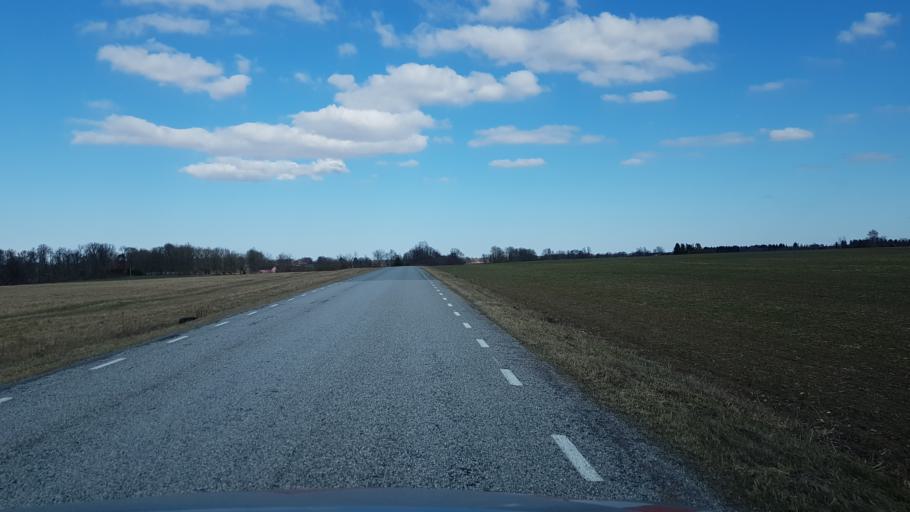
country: EE
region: Laeaene-Virumaa
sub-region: Kadrina vald
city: Kadrina
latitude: 59.3136
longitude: 26.2418
